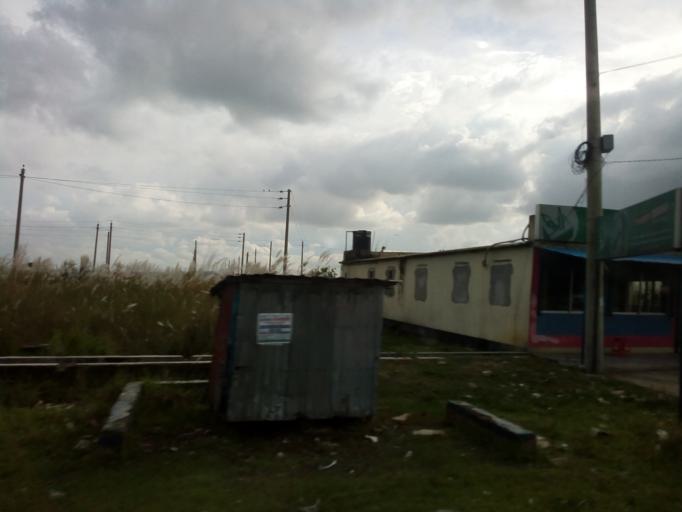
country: BD
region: Dhaka
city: Tungi
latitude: 23.8678
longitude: 90.3684
